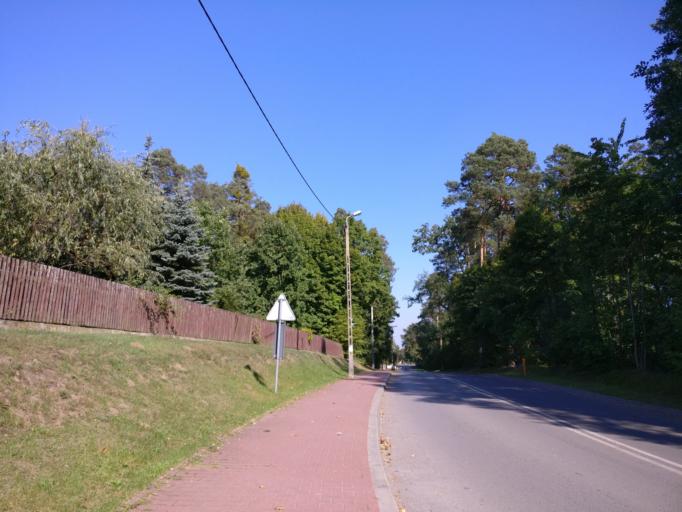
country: PL
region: Masovian Voivodeship
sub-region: Powiat kozienicki
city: Garbatka-Letnisko
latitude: 51.4933
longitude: 21.6245
